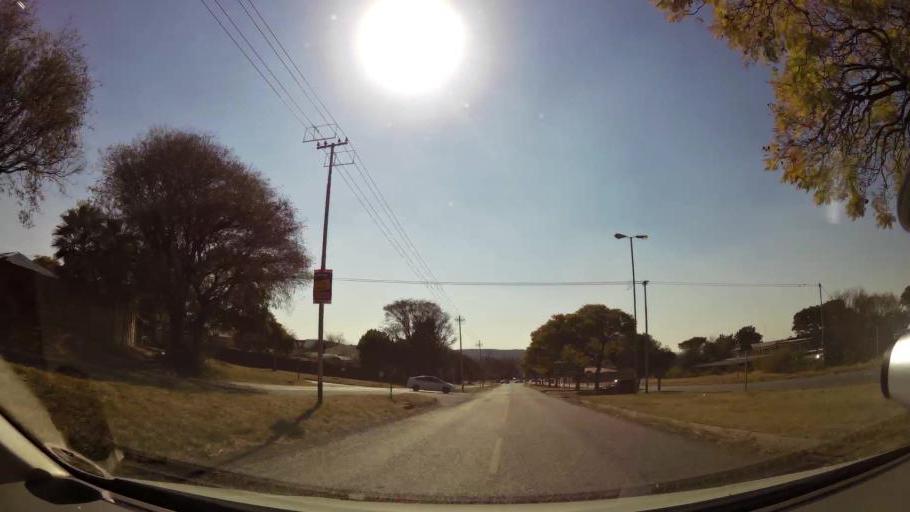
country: ZA
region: Gauteng
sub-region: City of Tshwane Metropolitan Municipality
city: Pretoria
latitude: -25.7511
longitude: 28.1454
